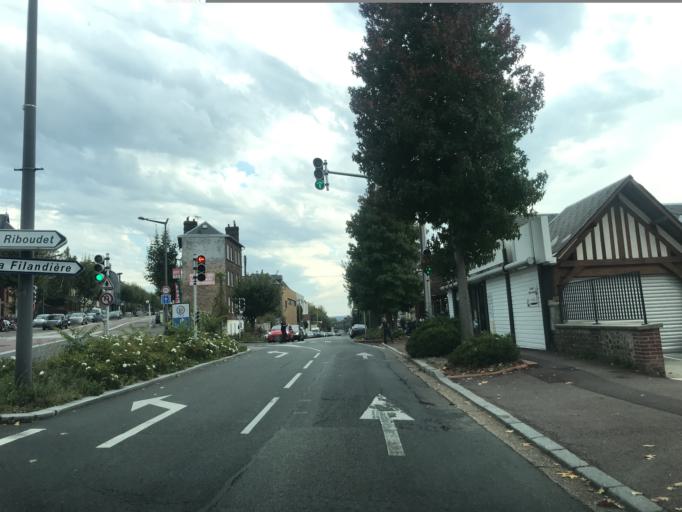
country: FR
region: Haute-Normandie
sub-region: Departement de la Seine-Maritime
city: Deville-les-Rouen
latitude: 49.4579
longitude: 1.0558
